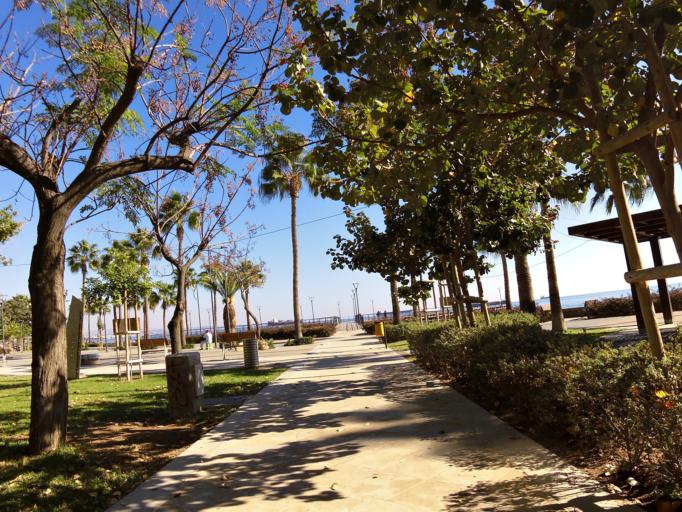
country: CY
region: Limassol
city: Limassol
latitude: 34.6723
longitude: 33.0447
